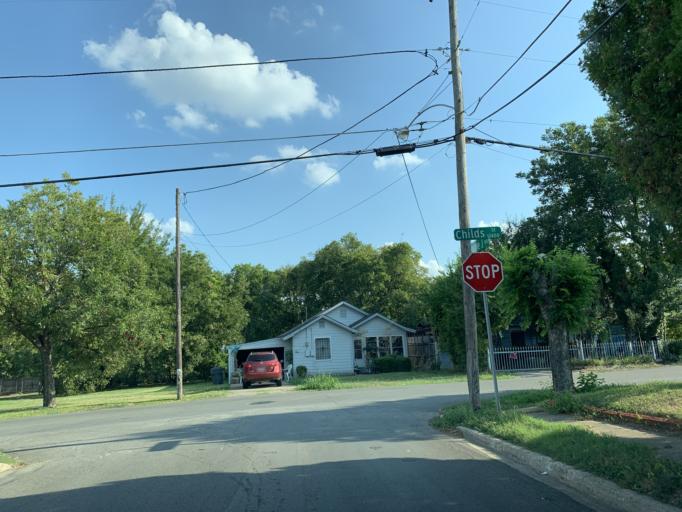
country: US
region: Texas
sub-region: Dallas County
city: Dallas
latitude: 32.7432
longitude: -96.7898
